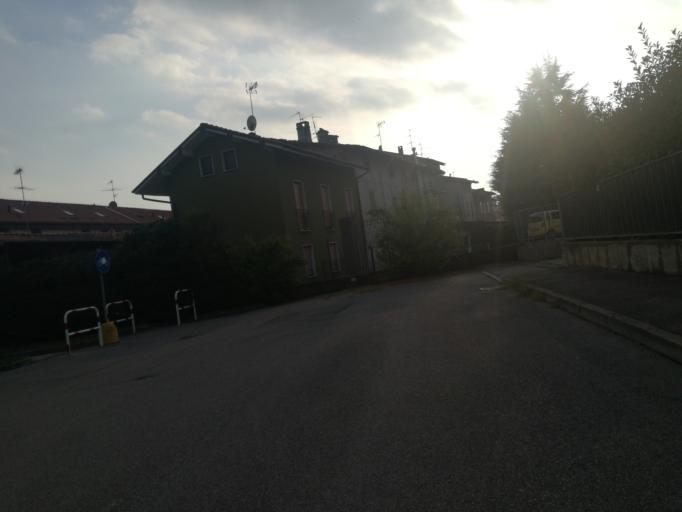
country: IT
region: Lombardy
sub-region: Provincia di Monza e Brianza
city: Porto d'Adda
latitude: 45.6486
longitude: 9.4688
